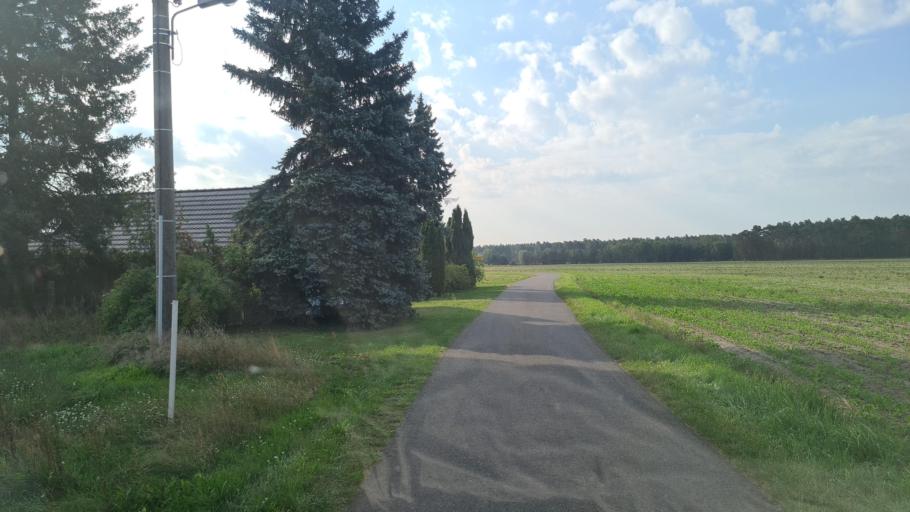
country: DE
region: Brandenburg
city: Neupetershain
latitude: 51.6486
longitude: 14.1770
